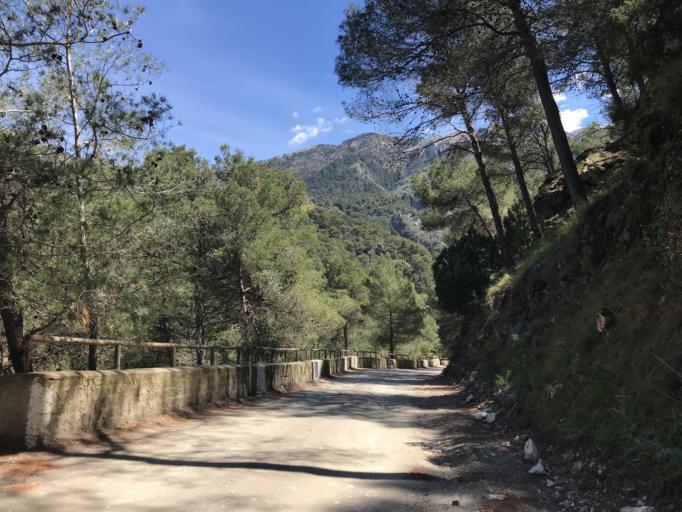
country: ES
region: Andalusia
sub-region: Provincia de Malaga
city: Alcaucin
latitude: 36.9159
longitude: -4.0954
